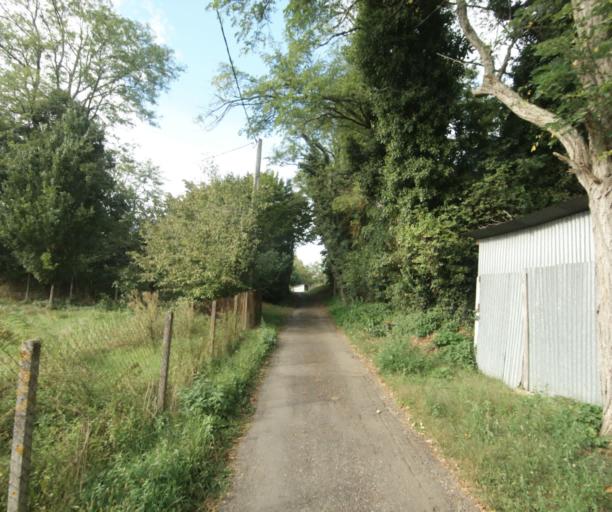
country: FR
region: Midi-Pyrenees
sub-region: Departement du Gers
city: Cazaubon
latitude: 43.8679
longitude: -0.1036
